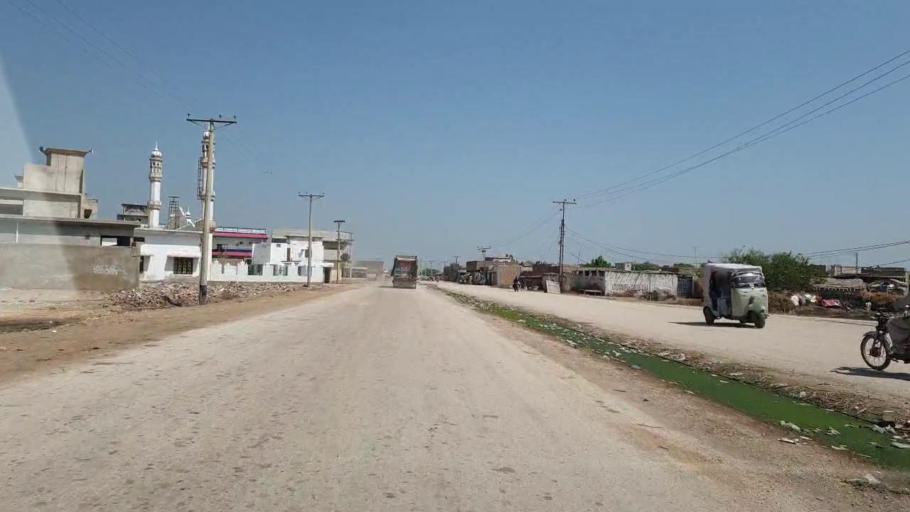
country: PK
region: Sindh
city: Hyderabad
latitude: 25.4279
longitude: 68.3947
